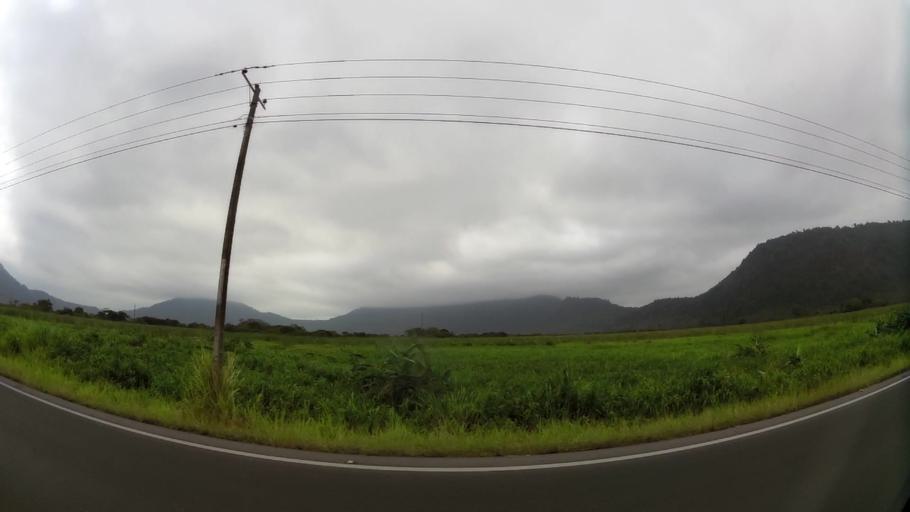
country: EC
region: Guayas
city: Naranjal
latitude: -2.4335
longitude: -79.6263
